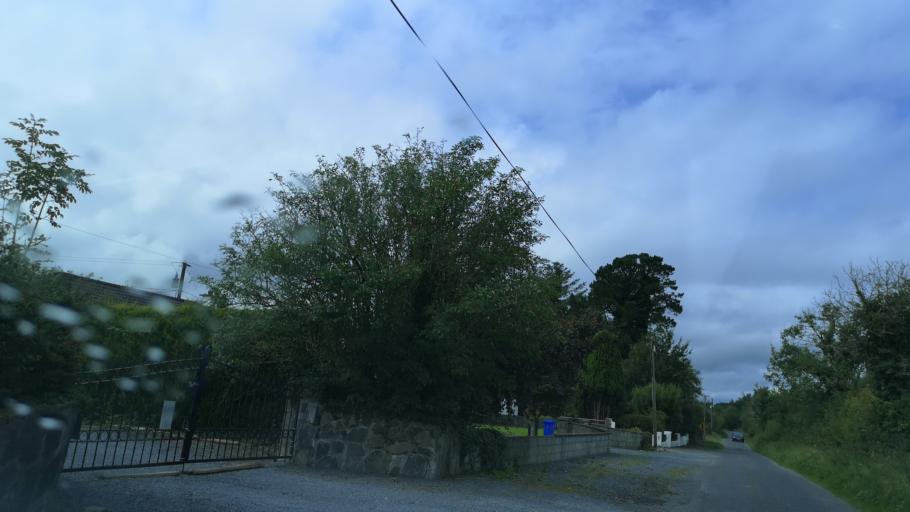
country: IE
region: Connaught
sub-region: County Galway
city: Loughrea
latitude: 53.2969
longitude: -8.5912
